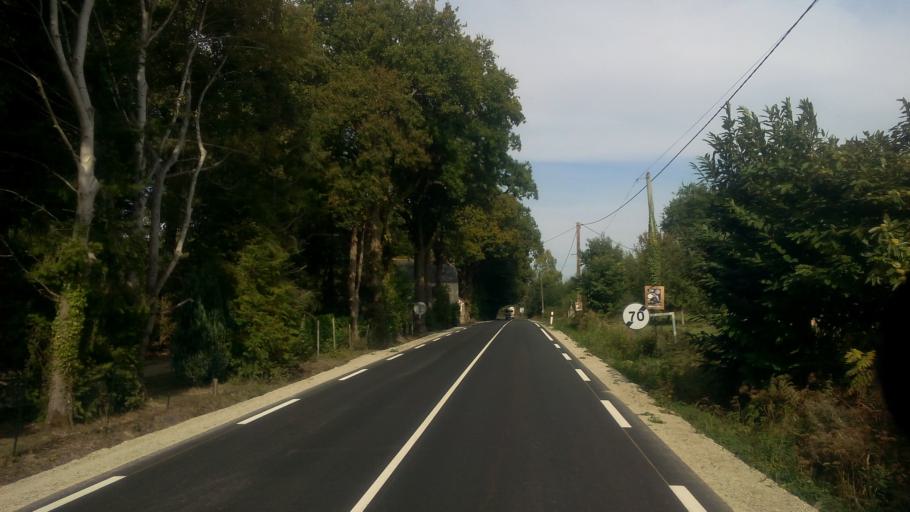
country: FR
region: Brittany
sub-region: Departement d'Ille-et-Vilaine
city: Bains-sur-Oust
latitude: 47.6898
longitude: -2.0855
